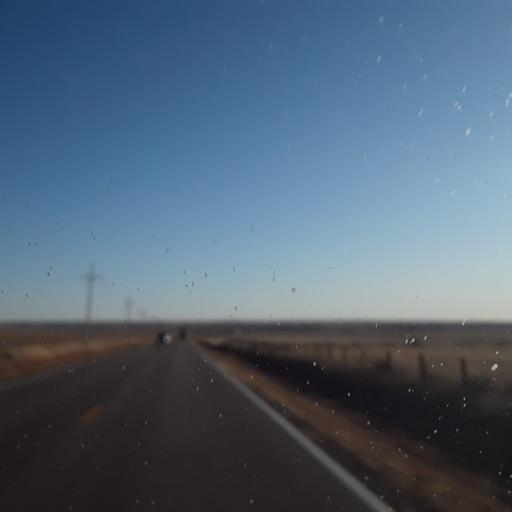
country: US
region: Kansas
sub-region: Wallace County
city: Sharon Springs
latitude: 38.9761
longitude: -101.7394
